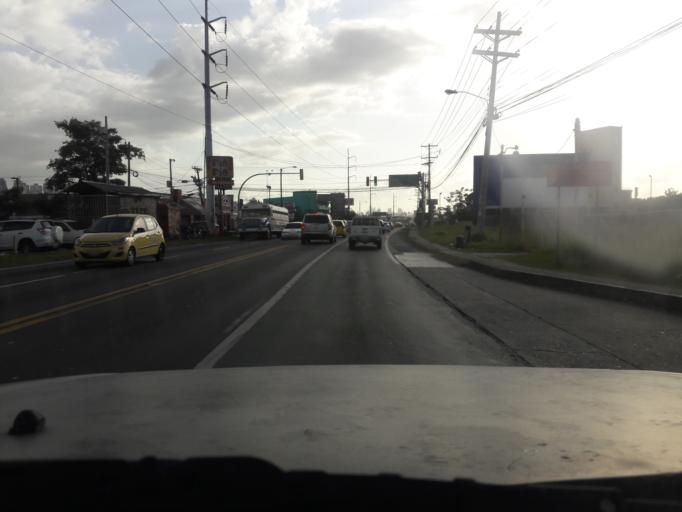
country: PA
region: Panama
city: San Miguelito
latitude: 9.0324
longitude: -79.4745
